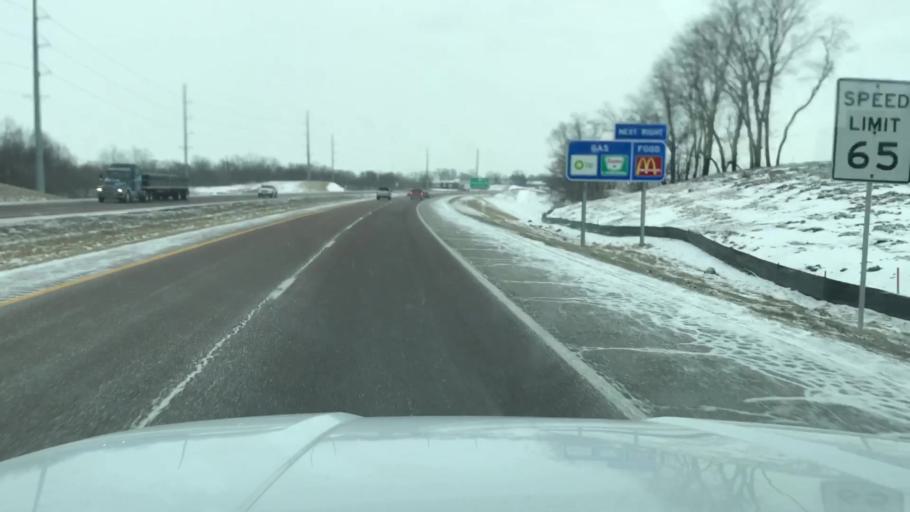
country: US
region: Missouri
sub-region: Buchanan County
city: Saint Joseph
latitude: 39.7511
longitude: -94.7831
